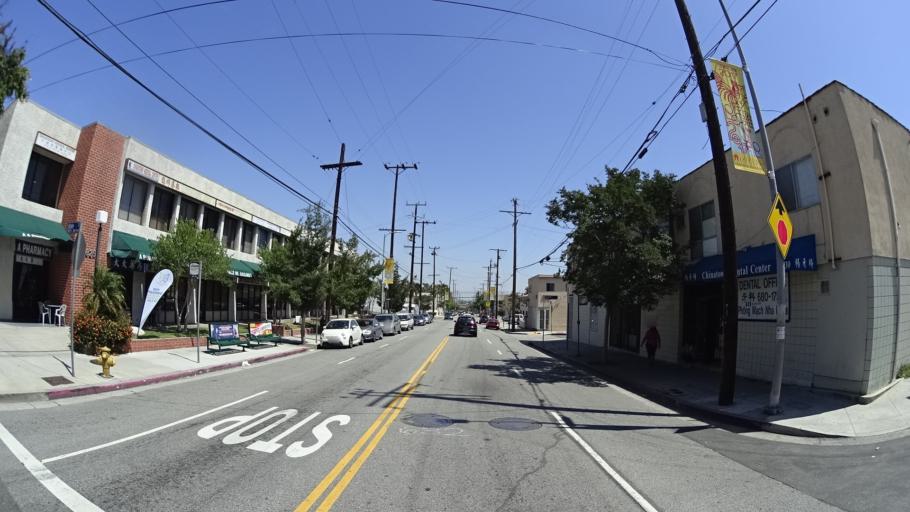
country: US
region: California
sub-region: Los Angeles County
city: Los Angeles
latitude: 34.0653
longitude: -118.2411
